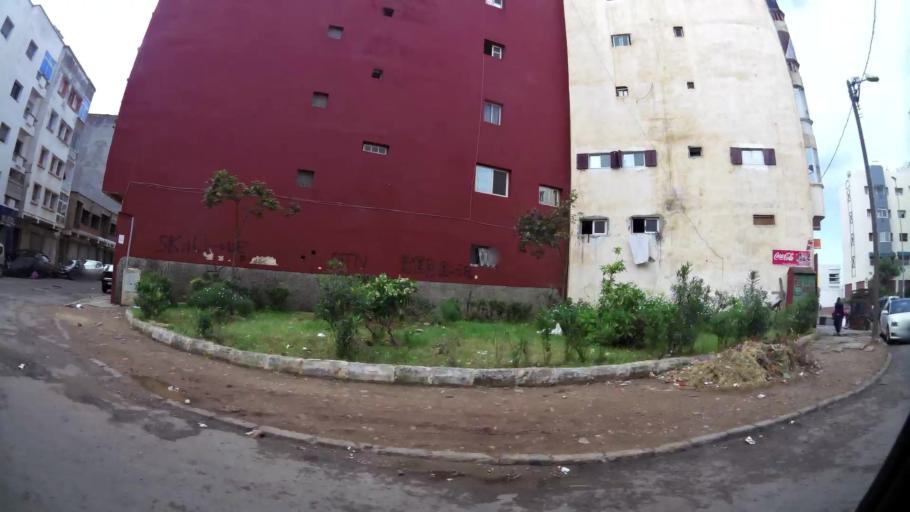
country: MA
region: Grand Casablanca
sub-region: Casablanca
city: Casablanca
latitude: 33.5684
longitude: -7.6717
